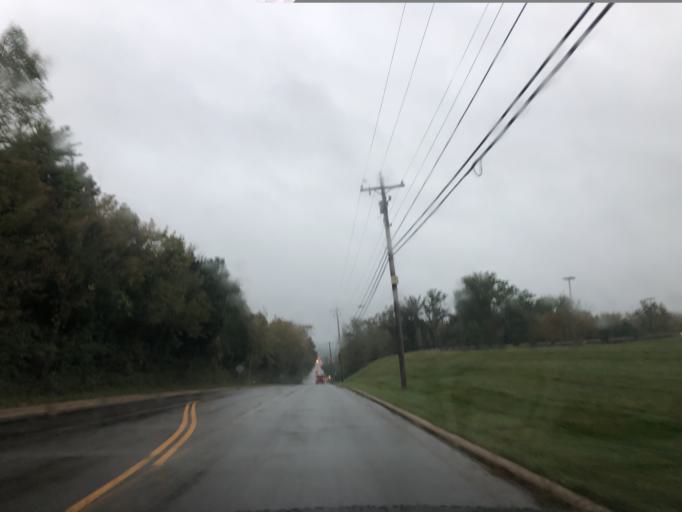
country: US
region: Ohio
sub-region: Hamilton County
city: Loveland
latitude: 39.2582
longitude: -84.2761
